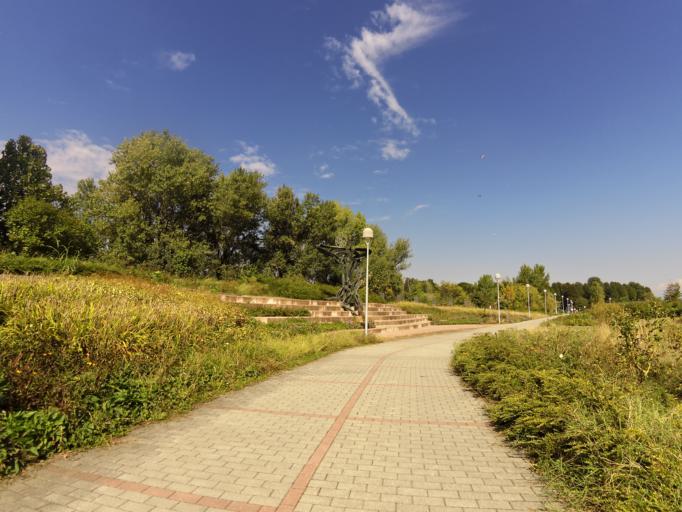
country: IT
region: Lombardy
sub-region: Citta metropolitana di Milano
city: Novegro-Tregarezzo-San Felice
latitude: 45.4607
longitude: 9.2862
